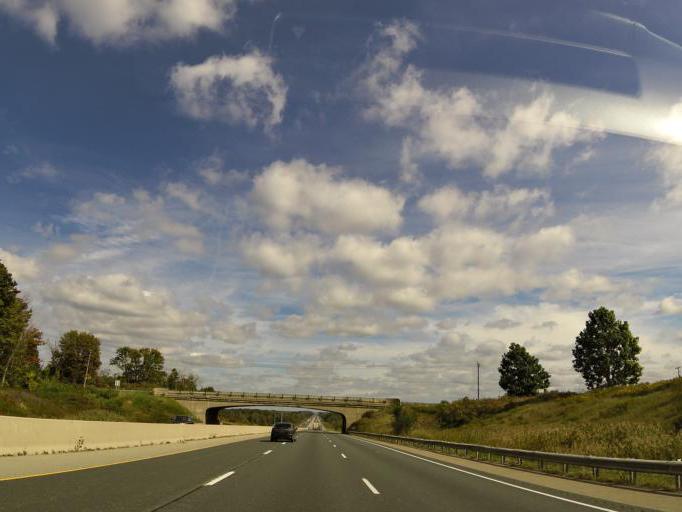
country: CA
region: Ontario
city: Dorchester
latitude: 42.9581
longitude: -81.0624
